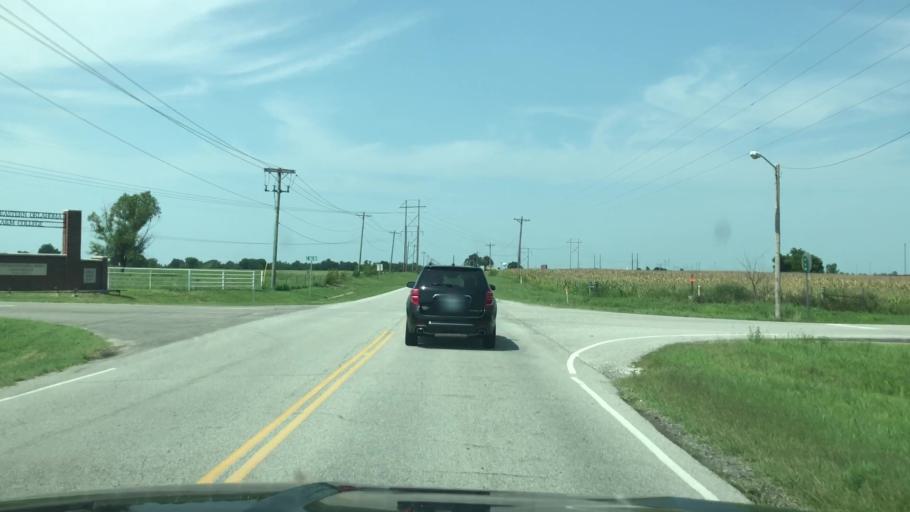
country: US
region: Oklahoma
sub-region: Ottawa County
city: Miami
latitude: 36.8854
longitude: -94.8417
